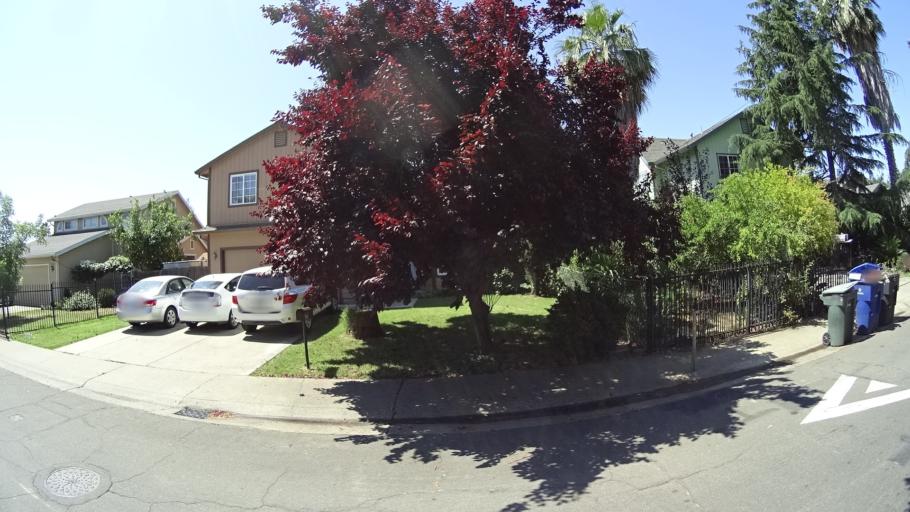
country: US
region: California
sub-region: Sacramento County
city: Florin
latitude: 38.5372
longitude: -121.4150
